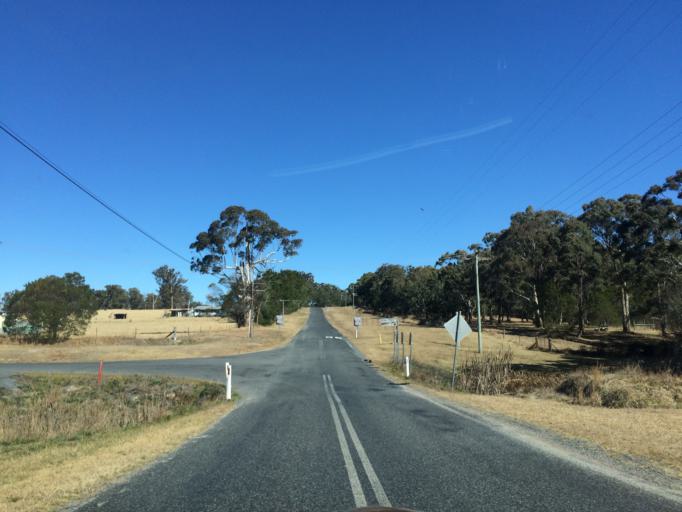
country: AU
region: Queensland
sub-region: Southern Downs
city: Stanthorpe
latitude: -28.6471
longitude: 152.0848
